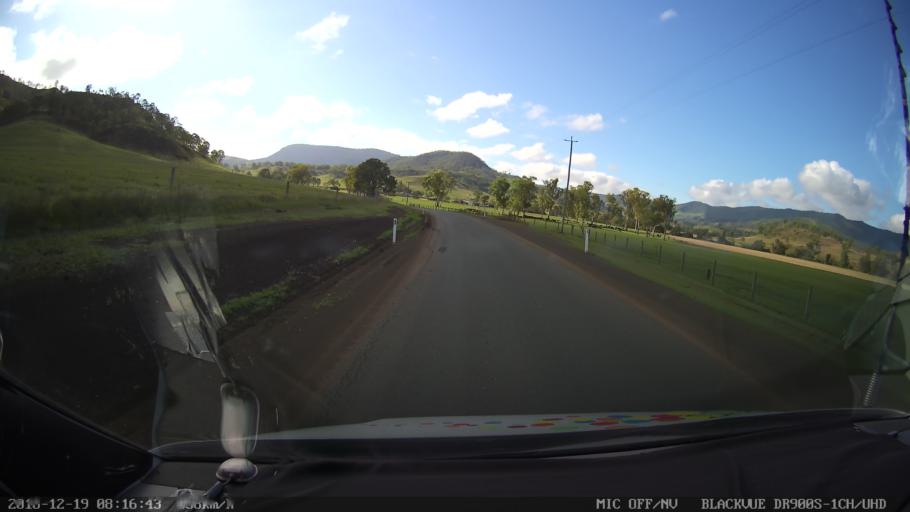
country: AU
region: New South Wales
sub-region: Kyogle
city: Kyogle
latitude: -28.2599
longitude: 152.9068
